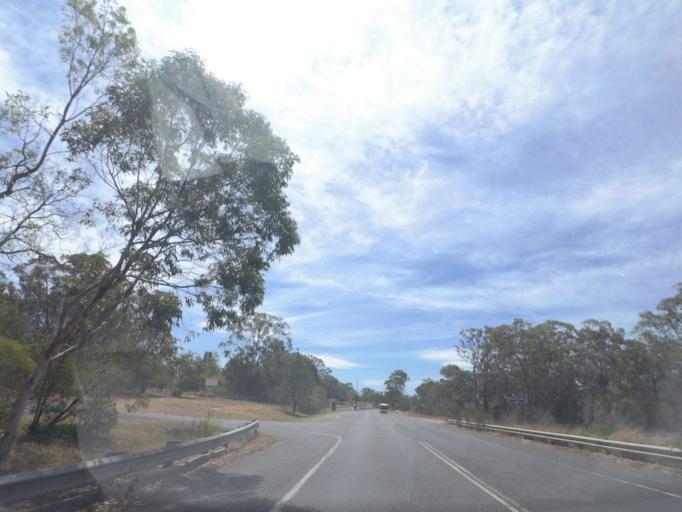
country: AU
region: New South Wales
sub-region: Wollondilly
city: Buxton
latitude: -34.2697
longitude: 150.5746
